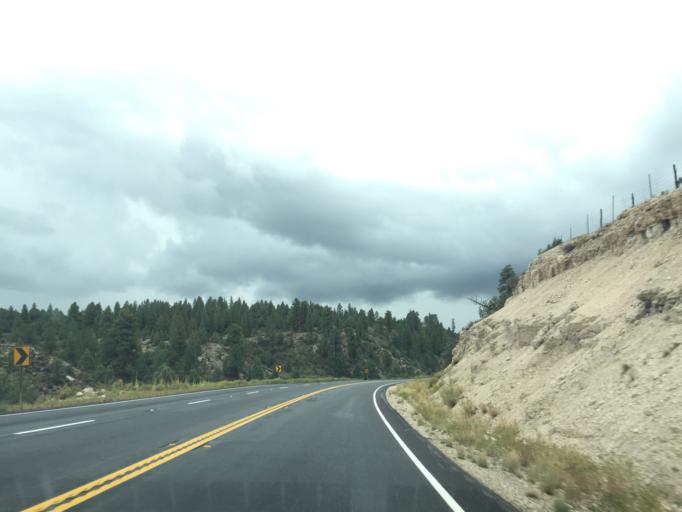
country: US
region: Utah
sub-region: Garfield County
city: Panguitch
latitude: 37.4747
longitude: -112.5132
